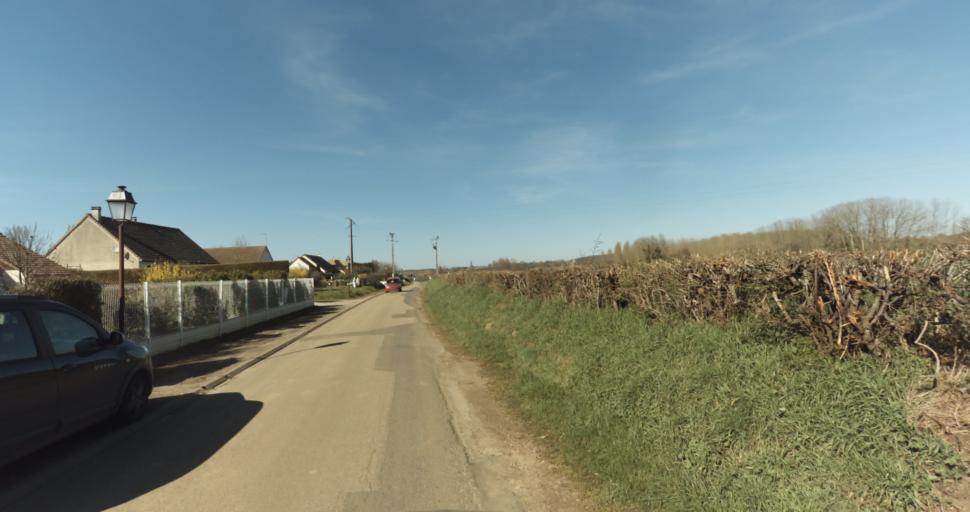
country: FR
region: Lower Normandy
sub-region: Departement du Calvados
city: Saint-Pierre-sur-Dives
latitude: 49.0435
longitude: -0.0263
